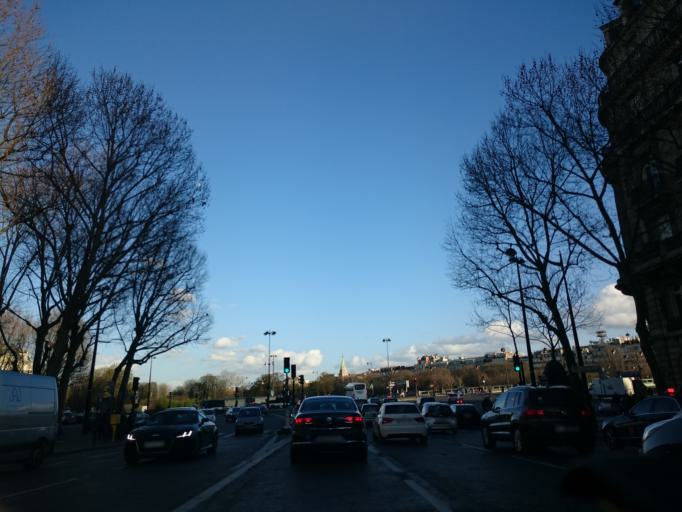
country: FR
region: Ile-de-France
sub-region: Departement des Hauts-de-Seine
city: Levallois-Perret
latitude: 48.8649
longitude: 2.3005
